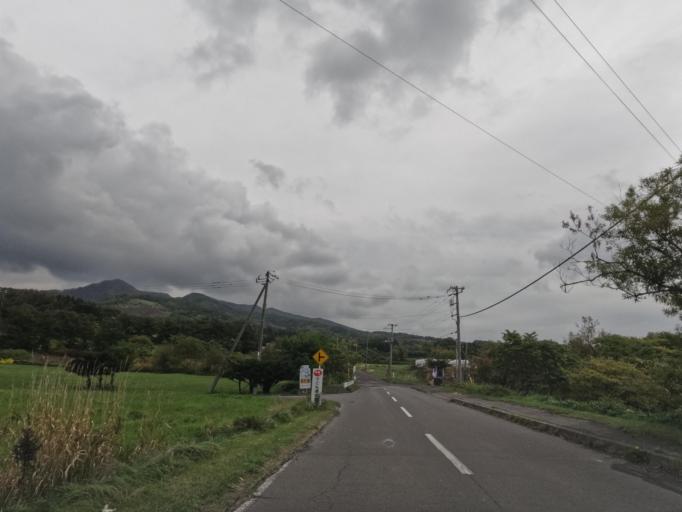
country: JP
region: Hokkaido
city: Date
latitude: 42.4549
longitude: 140.9059
